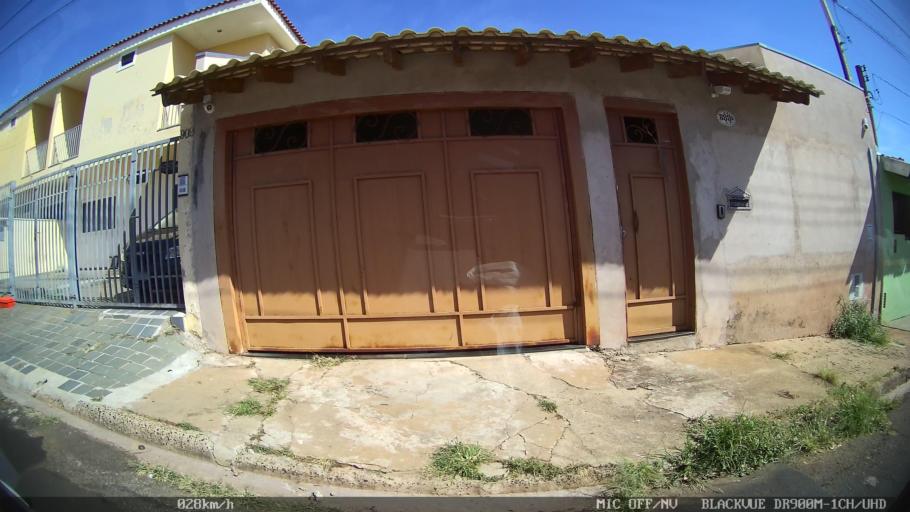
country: BR
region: Sao Paulo
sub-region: Franca
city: Franca
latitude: -20.5583
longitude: -47.3995
